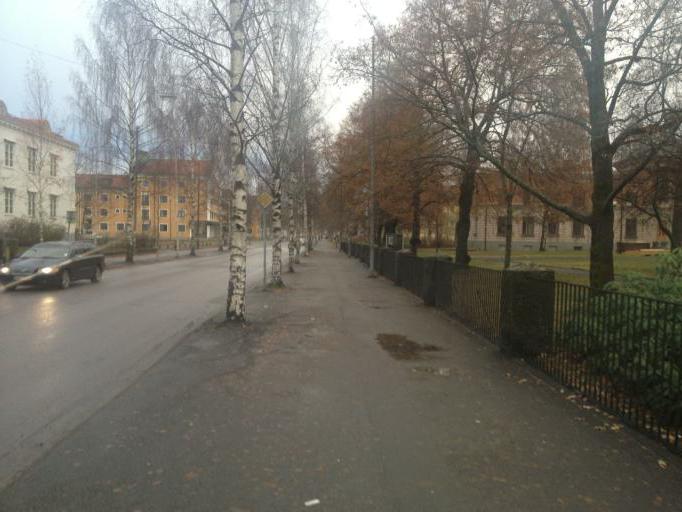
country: SE
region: Vaesterbotten
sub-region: Umea Kommun
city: Umea
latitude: 63.8233
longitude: 20.2722
